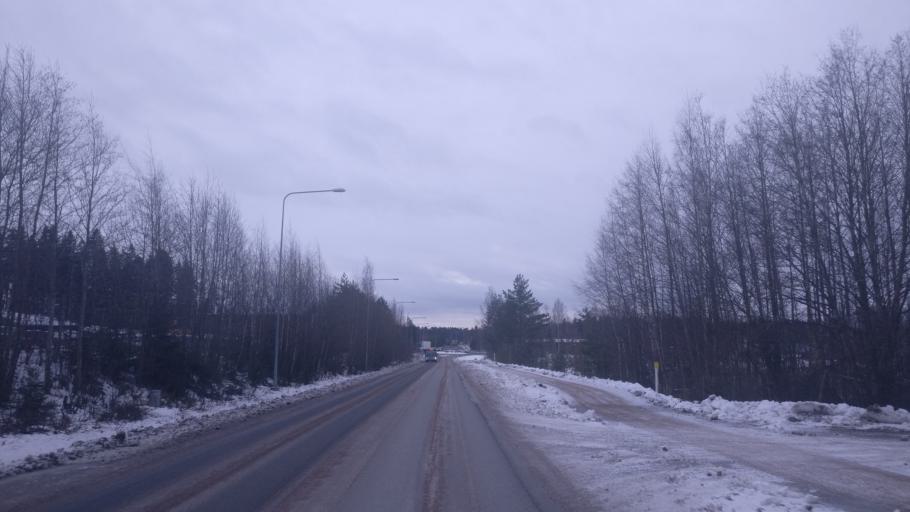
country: FI
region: Paijanne Tavastia
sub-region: Lahti
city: Lahti
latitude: 60.9686
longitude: 25.7257
